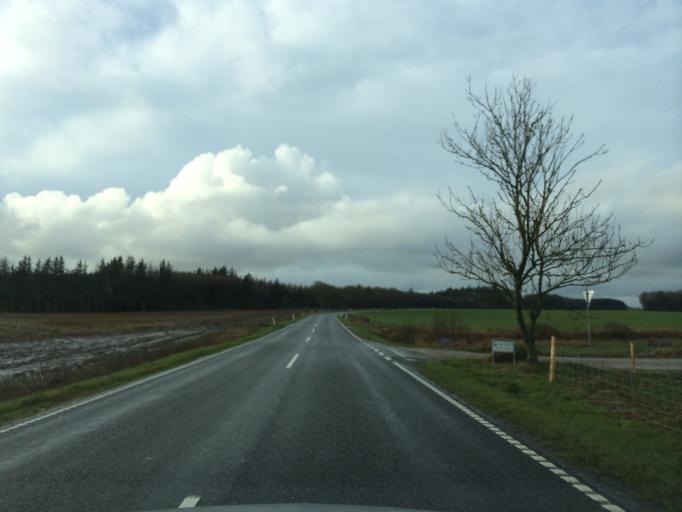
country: DK
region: Central Jutland
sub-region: Holstebro Kommune
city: Ulfborg
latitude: 56.1942
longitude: 8.3469
